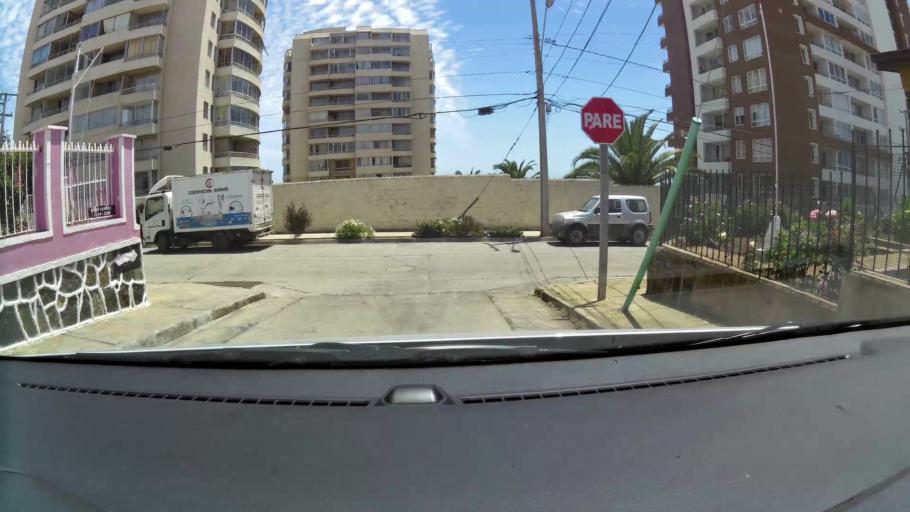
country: CL
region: Valparaiso
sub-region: Provincia de Valparaiso
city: Vina del Mar
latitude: -33.0488
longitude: -71.5797
